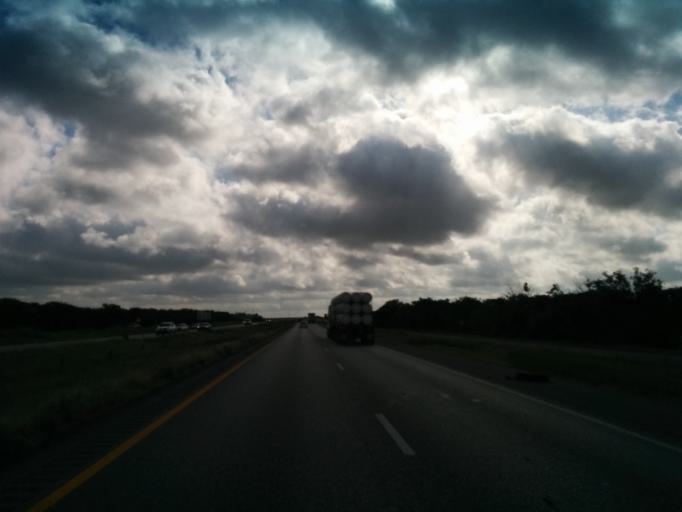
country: US
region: Texas
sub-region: Guadalupe County
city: Marion
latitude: 29.5254
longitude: -98.1217
